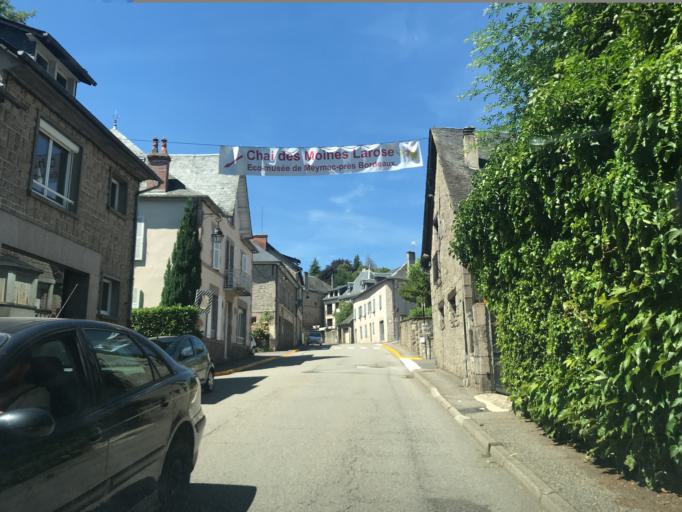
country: FR
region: Limousin
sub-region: Departement de la Correze
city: Meymac
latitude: 45.5358
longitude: 2.1456
